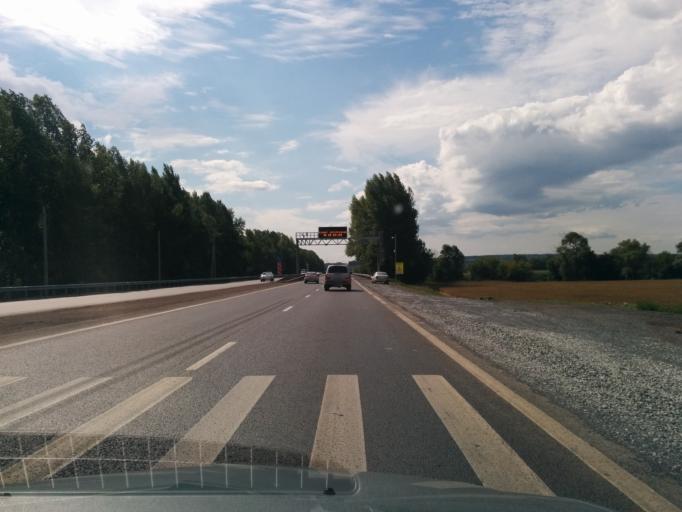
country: RU
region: Bashkortostan
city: Avdon
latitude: 54.5133
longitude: 55.8990
